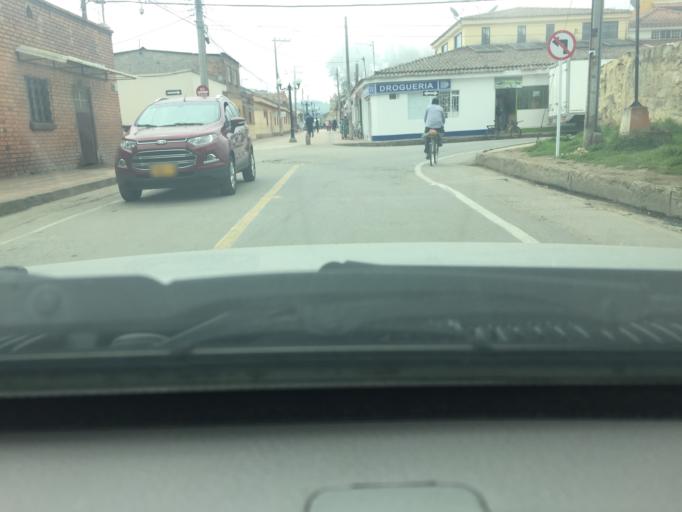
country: CO
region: Cundinamarca
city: Bojaca
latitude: 4.7338
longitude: -74.3416
